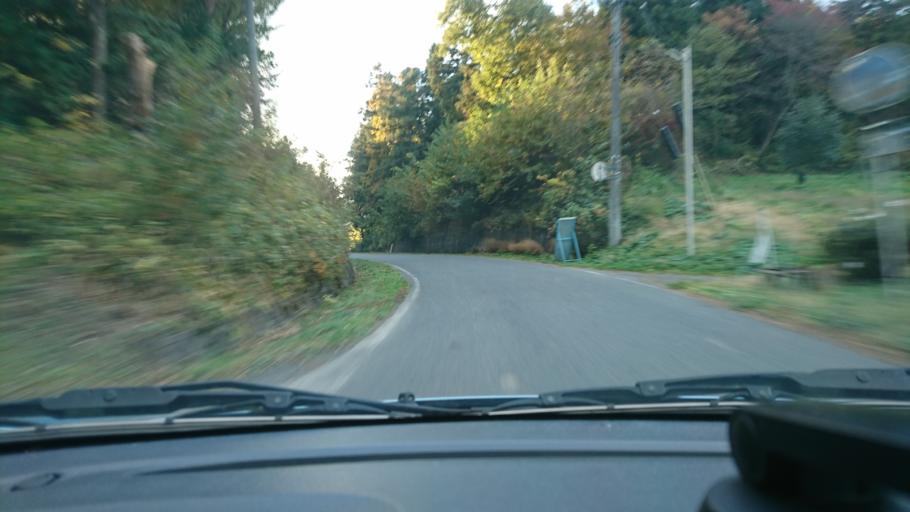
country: JP
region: Iwate
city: Ichinoseki
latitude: 38.7909
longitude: 141.1844
